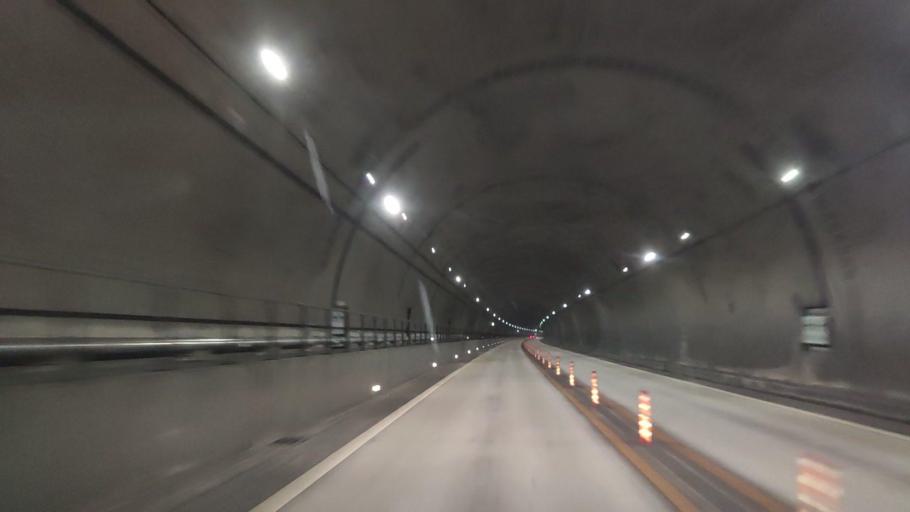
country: JP
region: Ehime
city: Hojo
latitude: 34.0792
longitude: 132.9763
